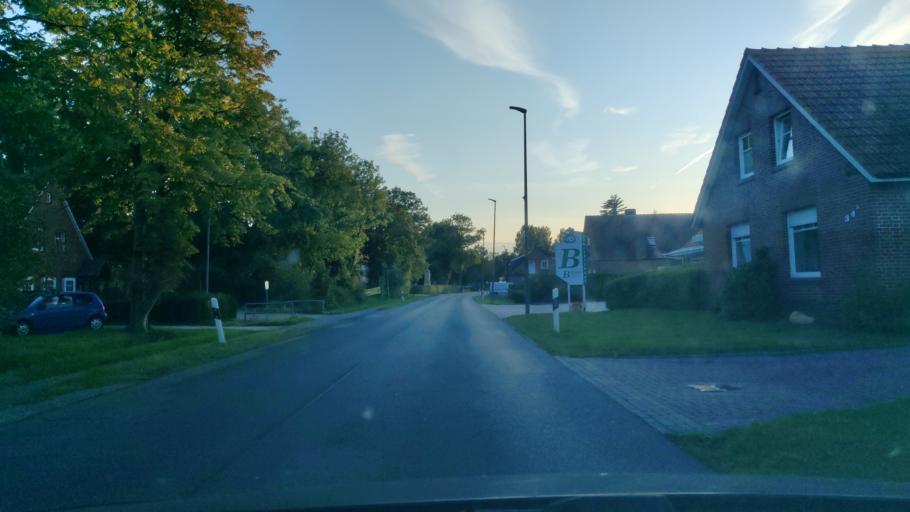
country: DE
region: Lower Saxony
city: Aurich
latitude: 53.4438
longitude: 7.4182
